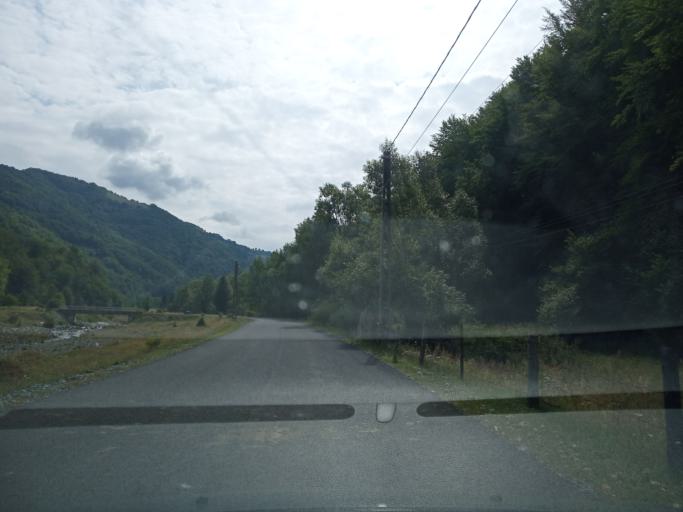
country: RO
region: Hunedoara
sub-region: Oras Petrila
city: Petrila
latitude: 45.4159
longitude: 23.4465
